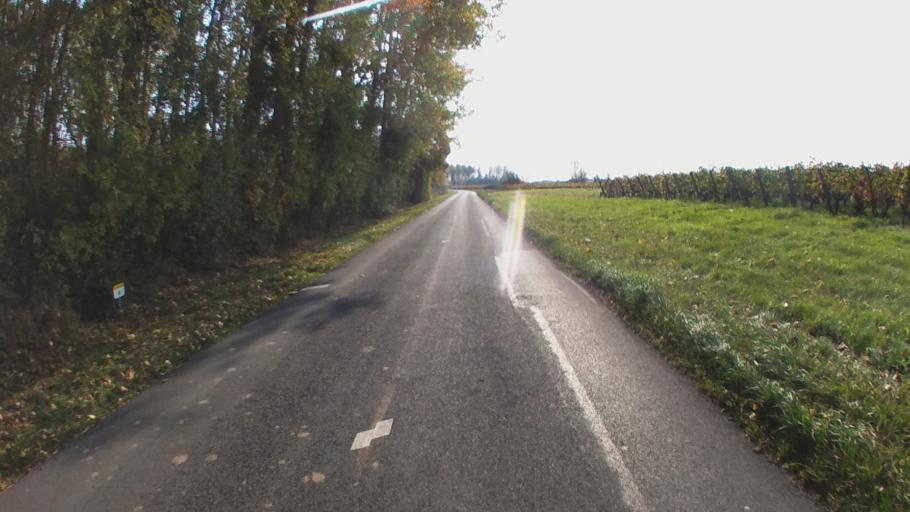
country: FR
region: Pays de la Loire
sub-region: Departement de Maine-et-Loire
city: Chace
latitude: 47.2137
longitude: -0.0905
